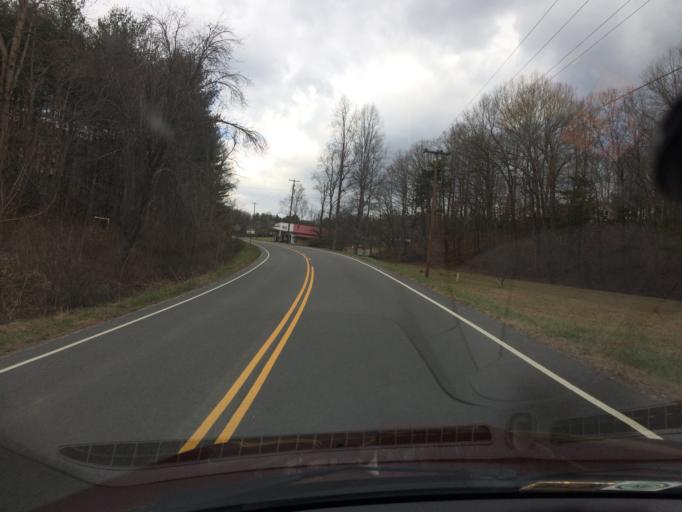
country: US
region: Virginia
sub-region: Patrick County
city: Stuart
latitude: 36.7258
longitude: -80.2403
